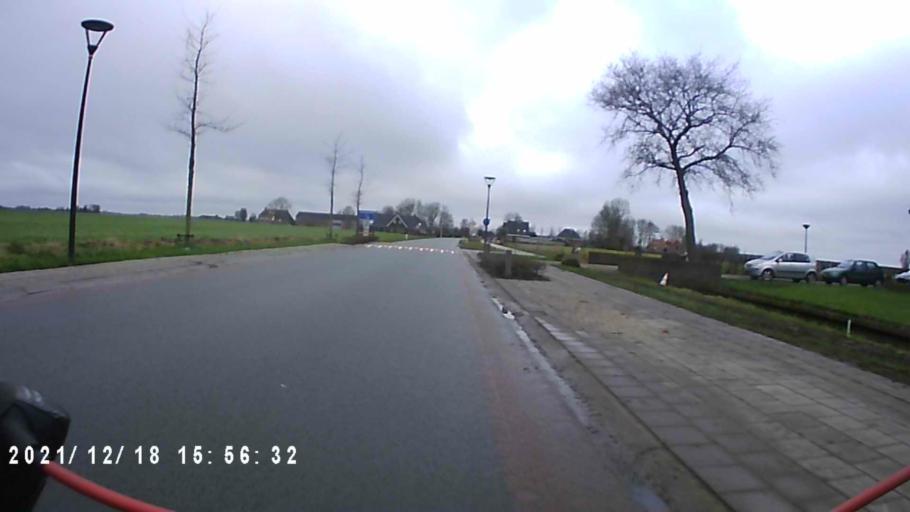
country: NL
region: Friesland
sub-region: Gemeente Dongeradeel
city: Anjum
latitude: 53.3324
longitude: 6.0984
